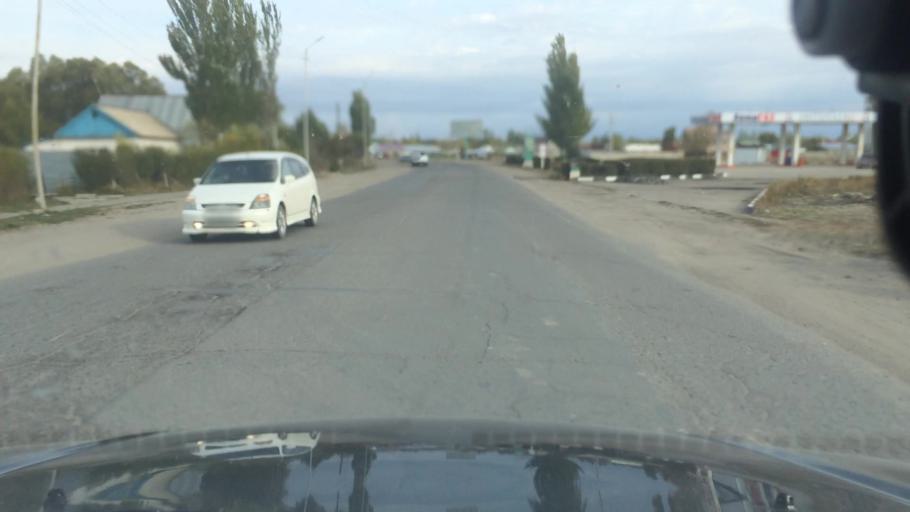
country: KG
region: Ysyk-Koel
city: Karakol
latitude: 42.5216
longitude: 78.3860
